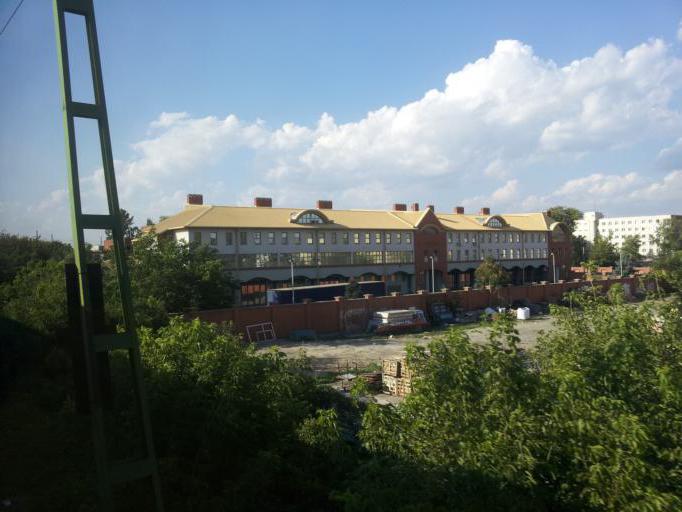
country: HU
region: Budapest
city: Budapest IX. keruelet
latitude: 47.4631
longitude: 19.0781
